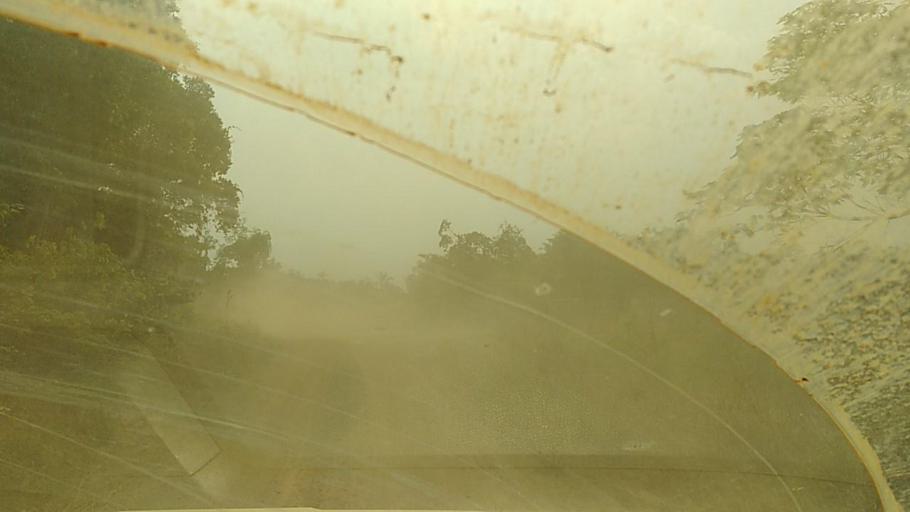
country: BR
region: Rondonia
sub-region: Porto Velho
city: Porto Velho
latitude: -8.7728
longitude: -63.1861
